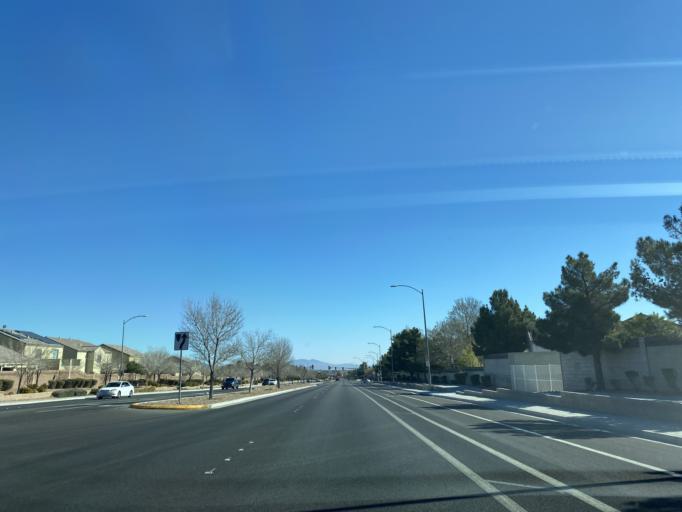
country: US
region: Nevada
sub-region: Clark County
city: Las Vegas
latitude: 36.3059
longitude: -115.2723
